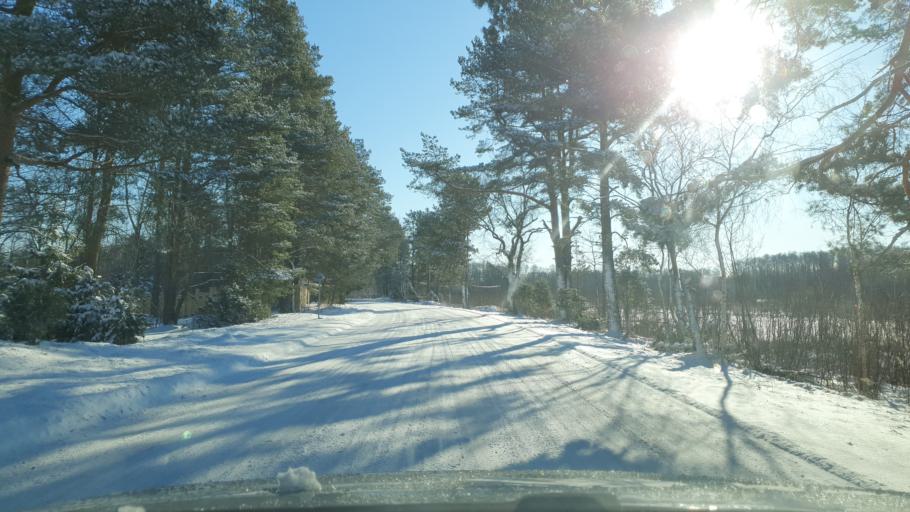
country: EE
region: Harju
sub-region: Kuusalu vald
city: Kuusalu
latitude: 59.4836
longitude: 25.4057
